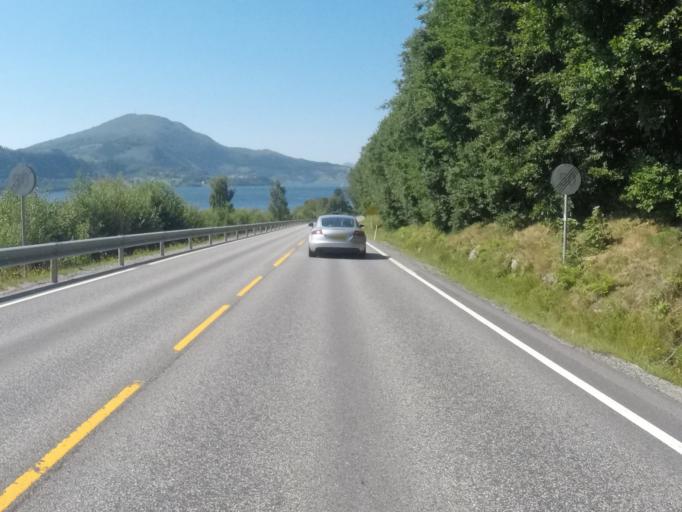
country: NO
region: More og Romsdal
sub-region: Orsta
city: Orsta
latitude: 62.2052
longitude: 6.1015
